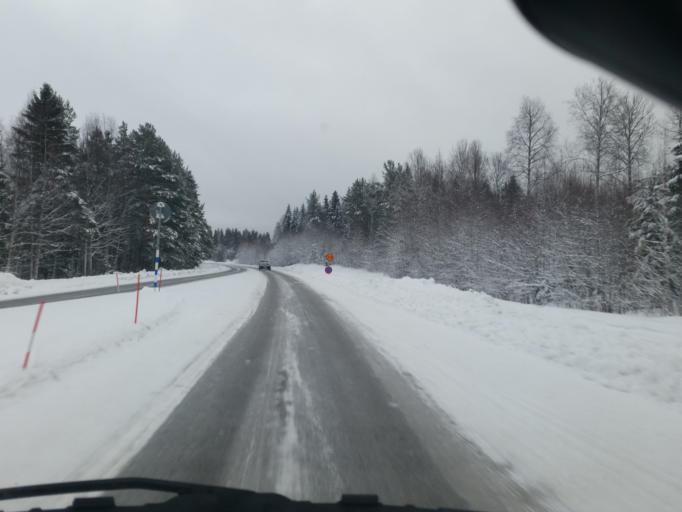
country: SE
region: Norrbotten
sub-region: Pitea Kommun
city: Bergsviken
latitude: 65.3171
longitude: 21.2926
